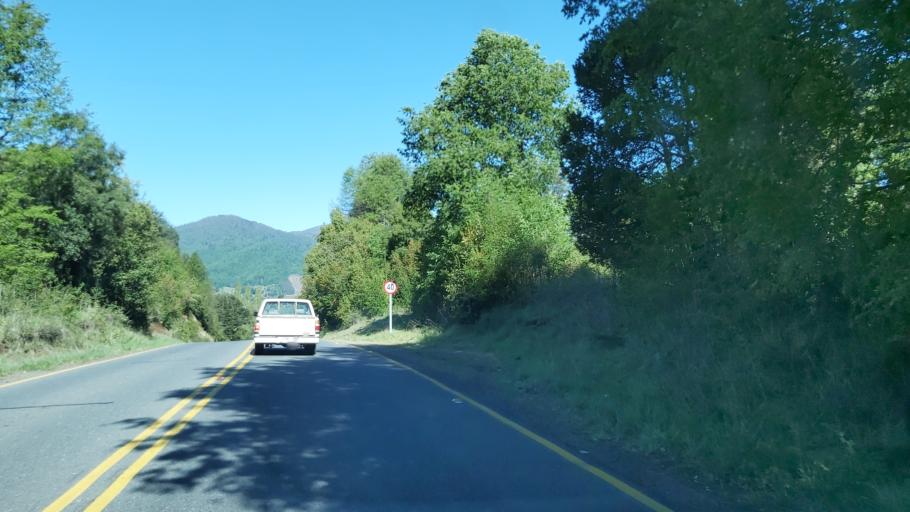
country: CL
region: Araucania
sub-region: Provincia de Cautin
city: Vilcun
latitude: -38.4887
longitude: -71.8290
